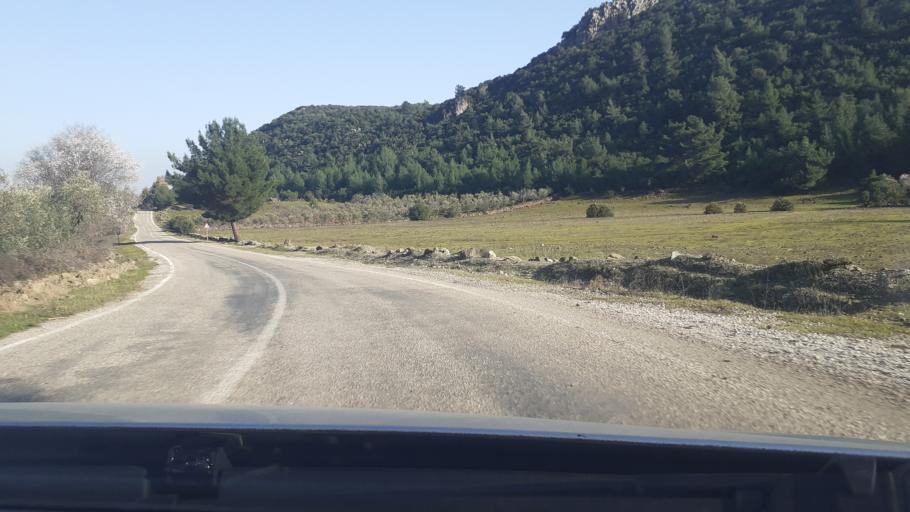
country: TR
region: Hatay
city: Aktepe
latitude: 36.7338
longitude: 36.4692
